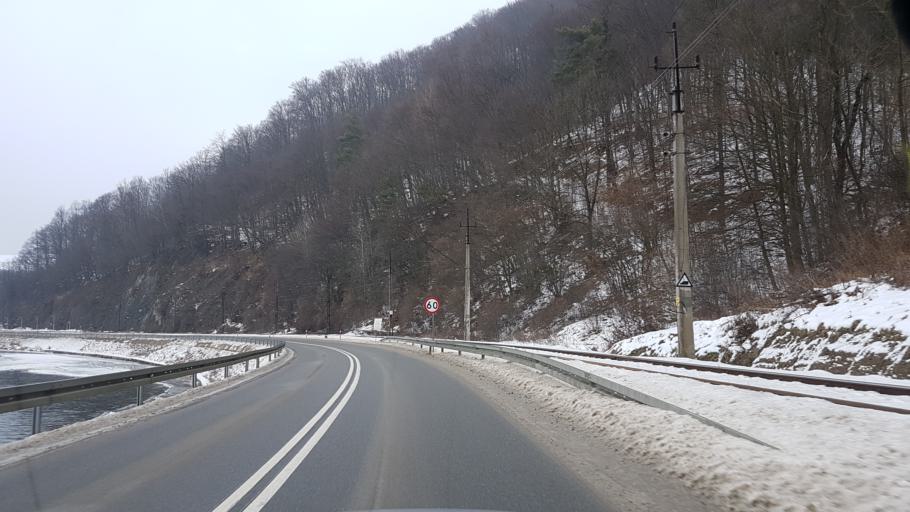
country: PL
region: Lesser Poland Voivodeship
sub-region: Powiat nowosadecki
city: Piwniczna-Zdroj
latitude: 49.3998
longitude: 20.7588
